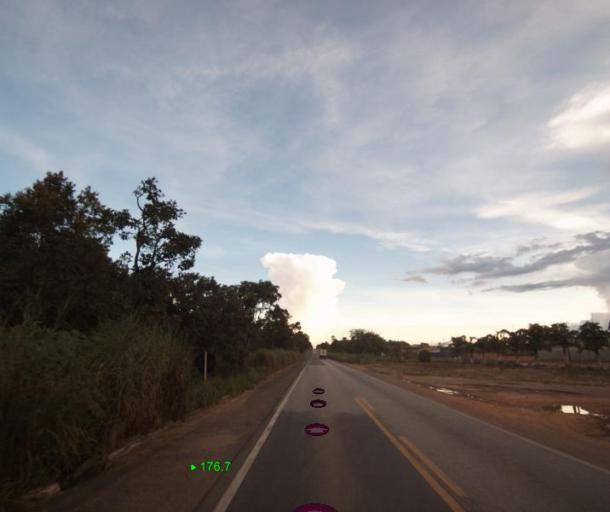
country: BR
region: Goias
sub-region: Uruacu
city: Uruacu
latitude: -14.3198
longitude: -49.1512
